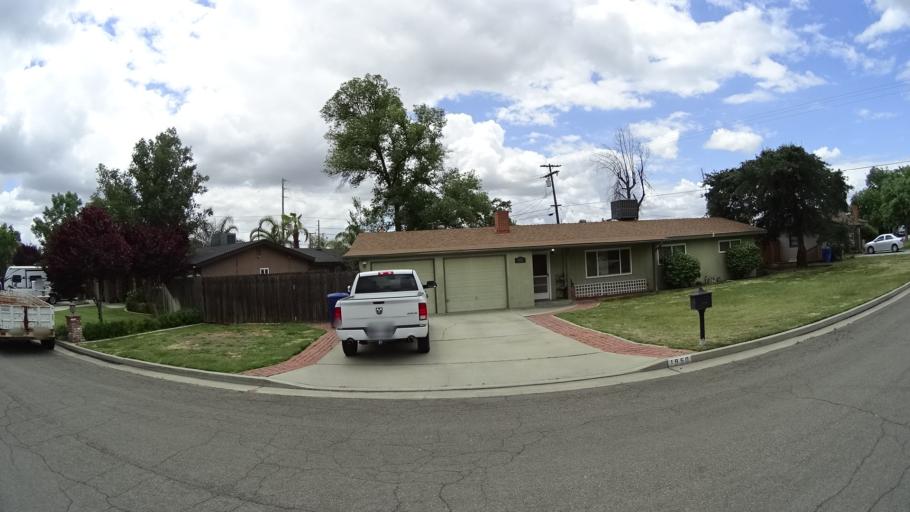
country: US
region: California
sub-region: Kings County
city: Hanford
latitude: 36.3470
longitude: -119.6532
